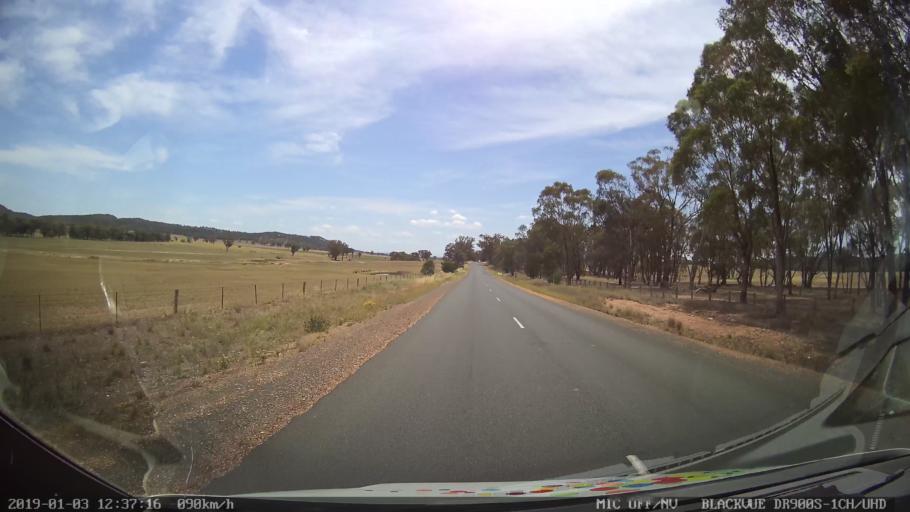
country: AU
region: New South Wales
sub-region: Weddin
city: Grenfell
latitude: -33.8447
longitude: 148.1826
